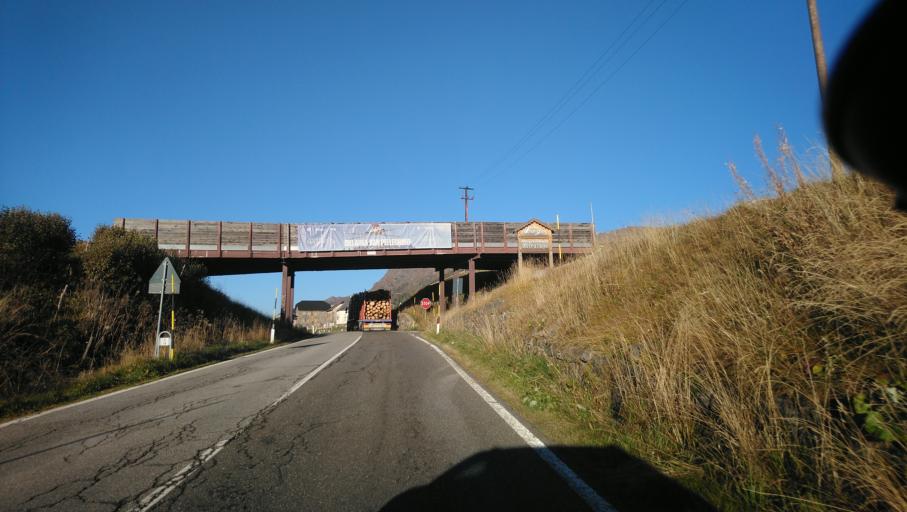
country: IT
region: Veneto
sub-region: Provincia di Belluno
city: Falcade Alto
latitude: 46.3785
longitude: 11.7972
